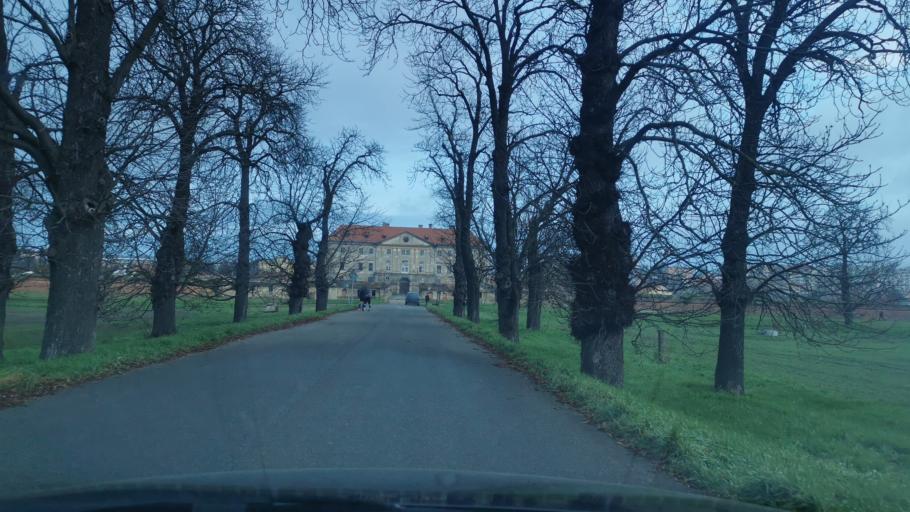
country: SK
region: Trnavsky
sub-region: Okres Skalica
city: Holic
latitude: 48.8079
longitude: 17.1536
